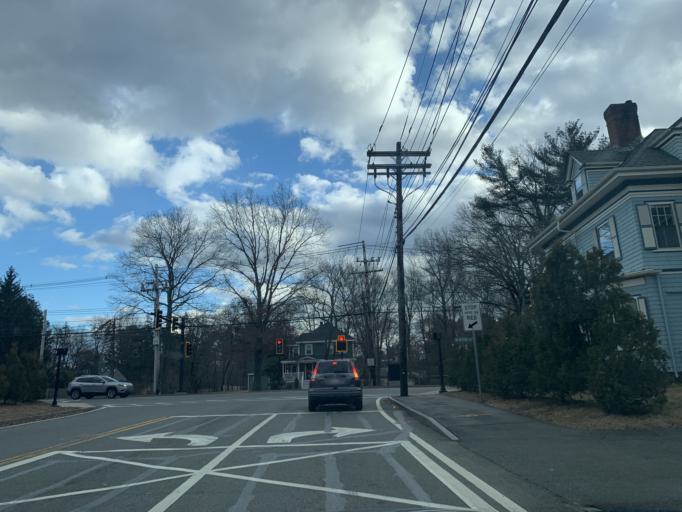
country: US
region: Massachusetts
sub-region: Norfolk County
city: Canton
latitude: 42.1731
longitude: -71.1386
